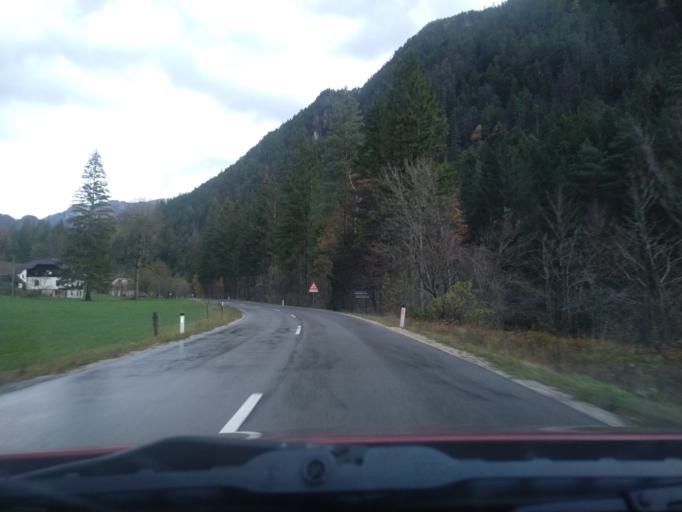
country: SI
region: Solcava
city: Solcava
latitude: 46.3934
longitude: 14.7131
